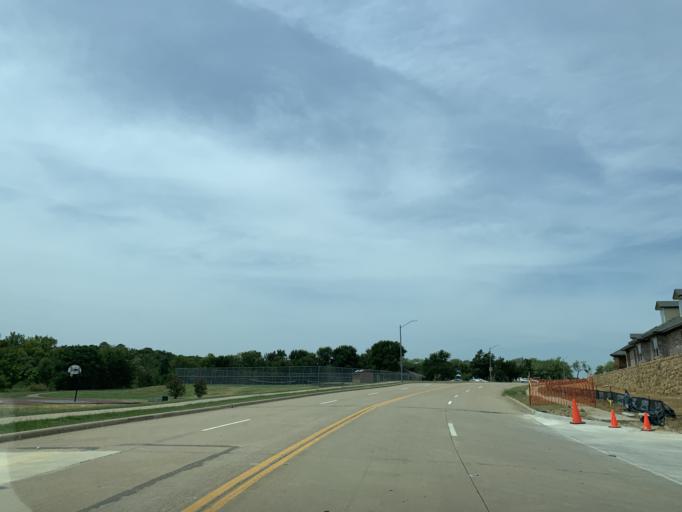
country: US
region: Texas
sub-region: Dallas County
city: Cedar Hill
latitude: 32.6572
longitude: -97.0020
